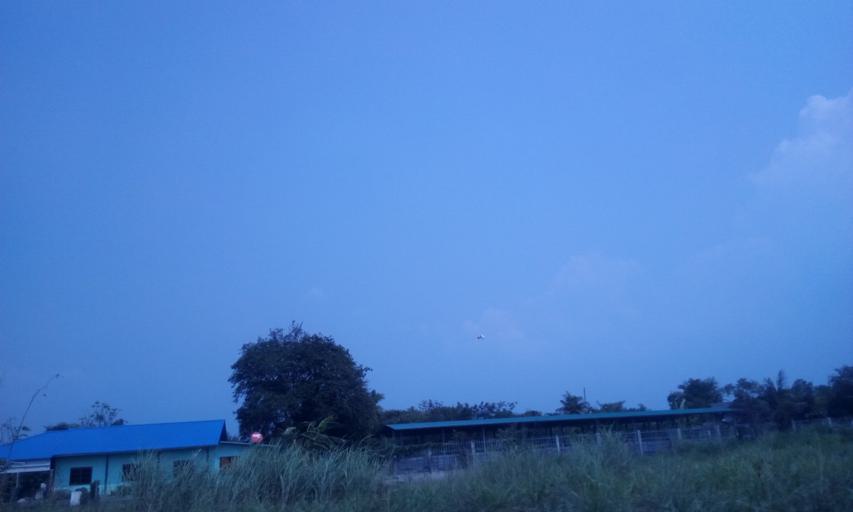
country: TH
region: Chon Buri
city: Phanat Nikhom
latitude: 13.4006
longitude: 101.1904
